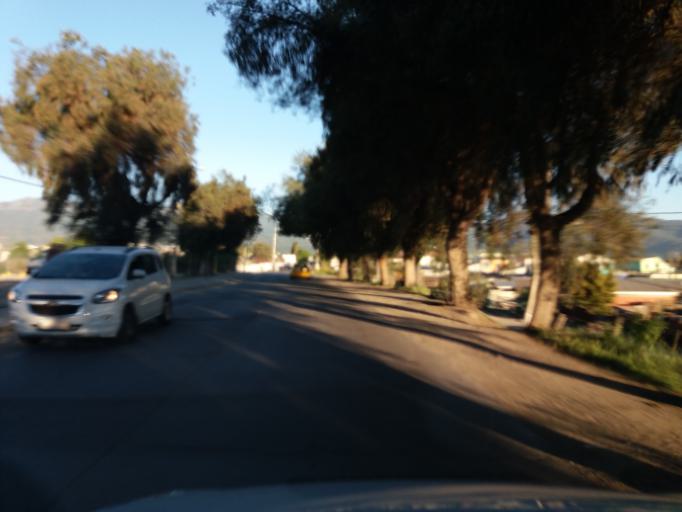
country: CL
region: Valparaiso
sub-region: Provincia de Quillota
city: Quillota
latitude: -32.8787
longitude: -71.2618
